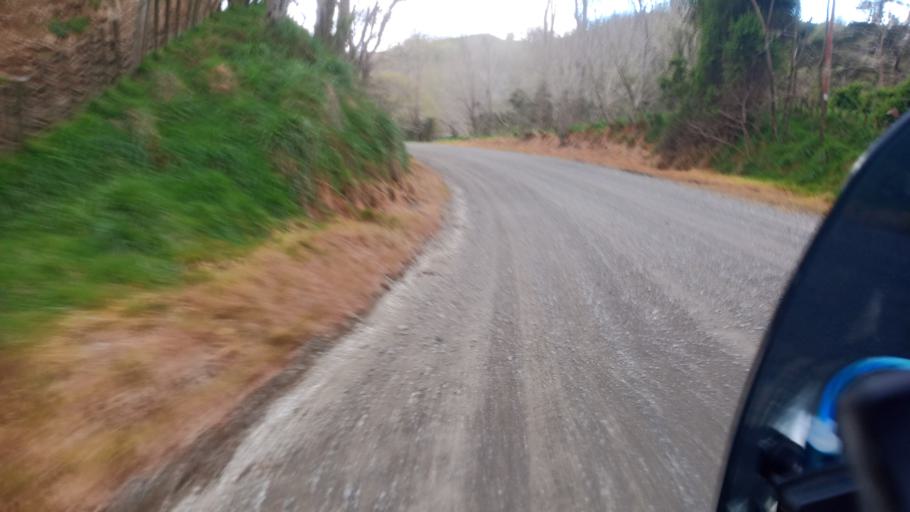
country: NZ
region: Gisborne
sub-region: Gisborne District
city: Gisborne
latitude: -38.2029
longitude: 178.2468
